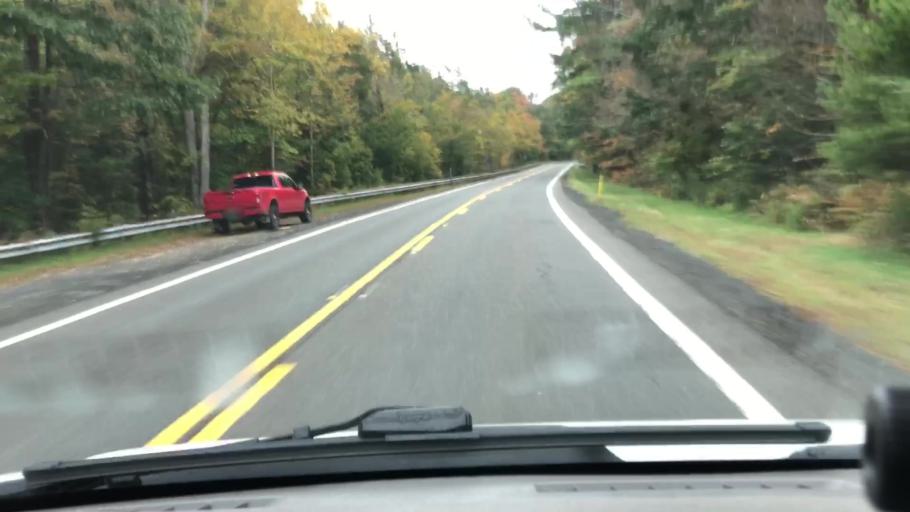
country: US
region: Massachusetts
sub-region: Hampshire County
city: Chesterfield
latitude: 42.3351
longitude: -72.8843
